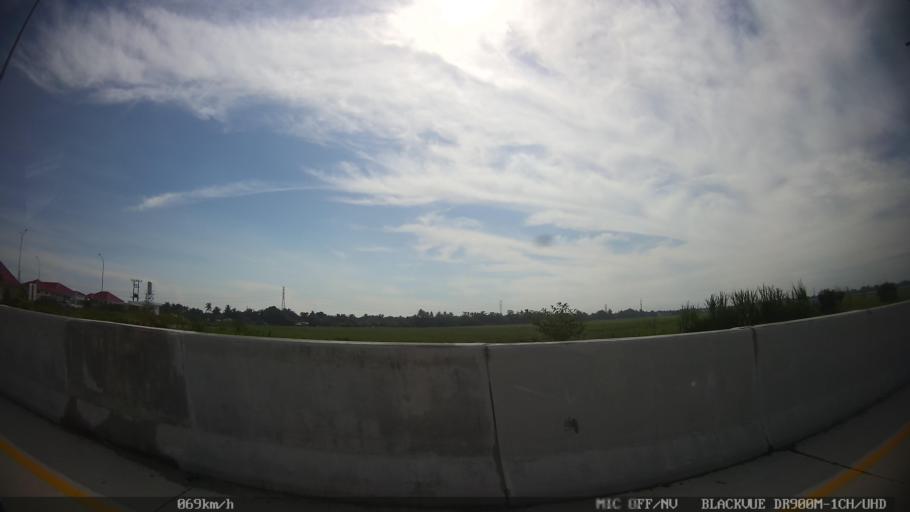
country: ID
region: North Sumatra
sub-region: Kabupaten Langkat
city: Stabat
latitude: 3.7166
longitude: 98.4938
